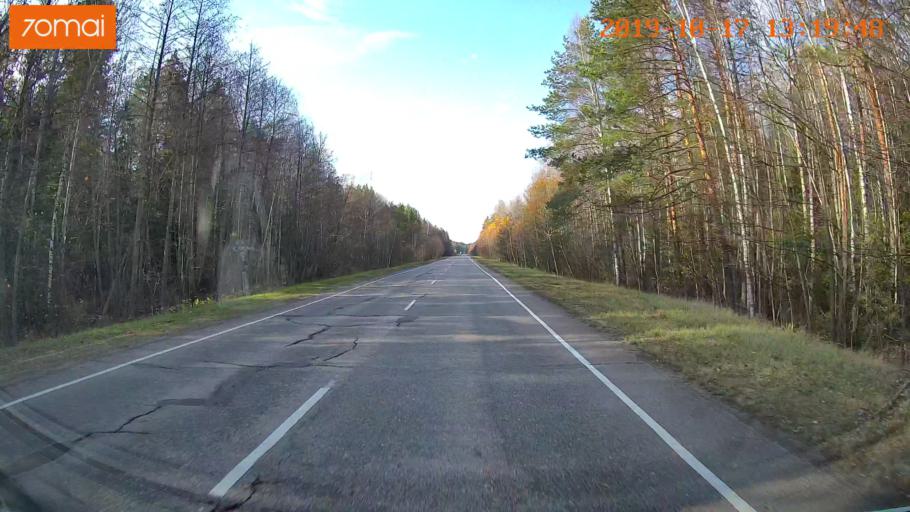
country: RU
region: Rjazan
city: Gus'-Zheleznyy
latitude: 55.0718
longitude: 41.0653
